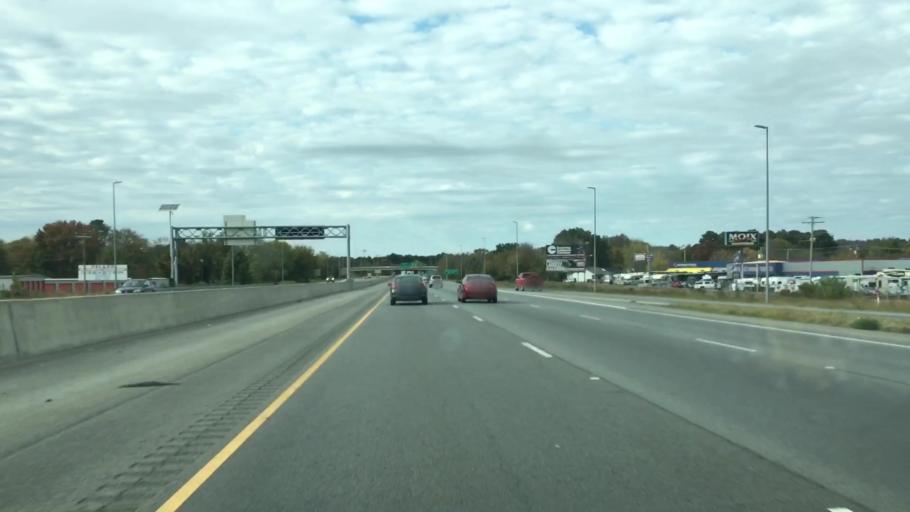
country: US
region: Arkansas
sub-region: Faulkner County
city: Conway
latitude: 35.0947
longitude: -92.4257
